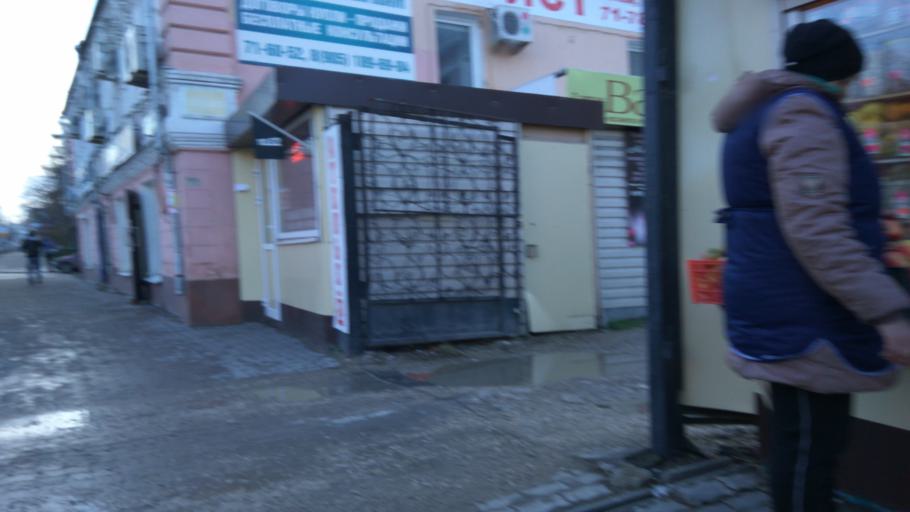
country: RU
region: Tula
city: Tula
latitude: 54.1983
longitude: 37.6113
